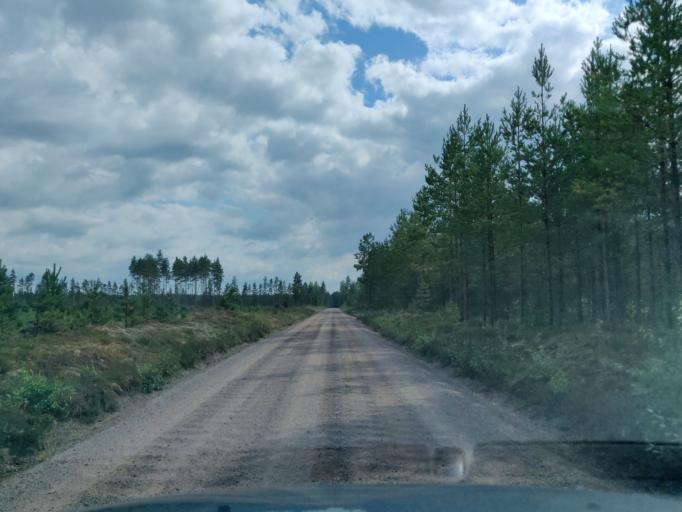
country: SE
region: Vaermland
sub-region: Hagfors Kommun
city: Hagfors
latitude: 59.9785
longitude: 13.5485
